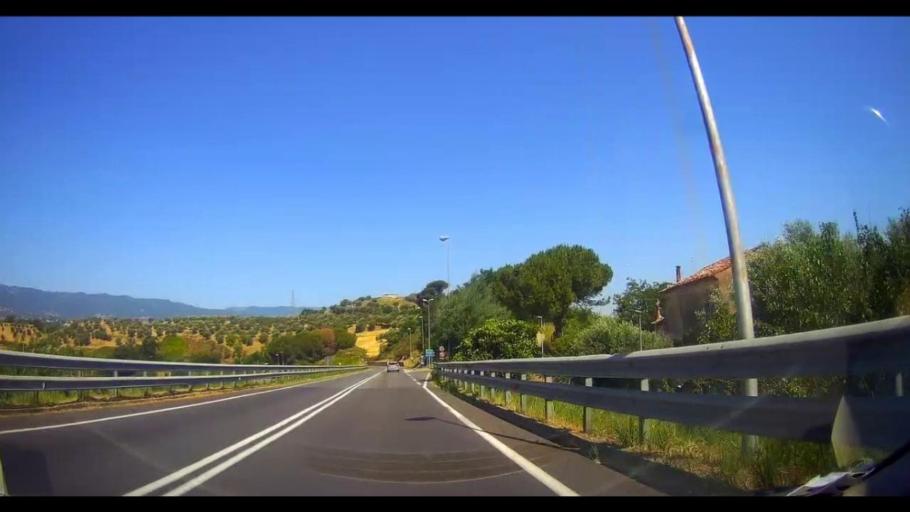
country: IT
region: Calabria
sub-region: Provincia di Cosenza
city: Cosenza
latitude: 39.2949
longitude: 16.2716
